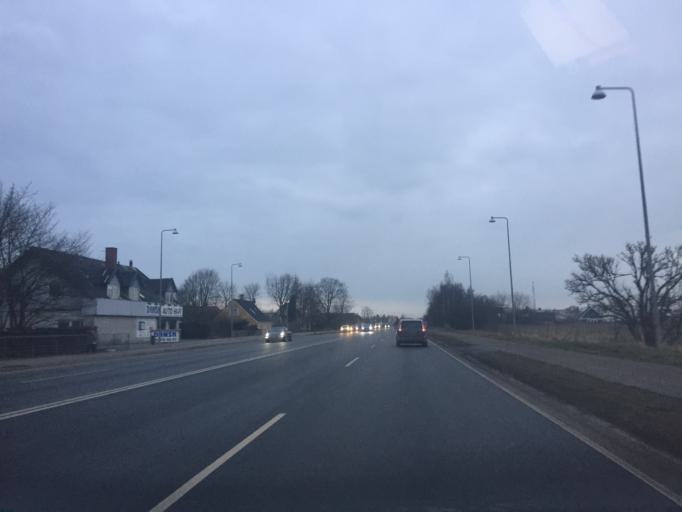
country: DK
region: Zealand
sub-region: Koge Kommune
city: Koge
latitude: 55.4941
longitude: 12.1923
